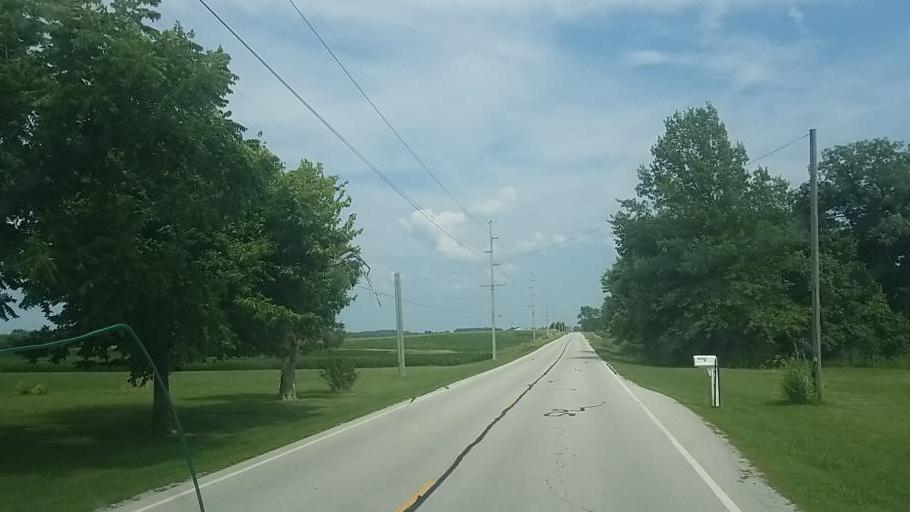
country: US
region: Ohio
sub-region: Hardin County
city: Forest
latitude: 40.7819
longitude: -83.5557
